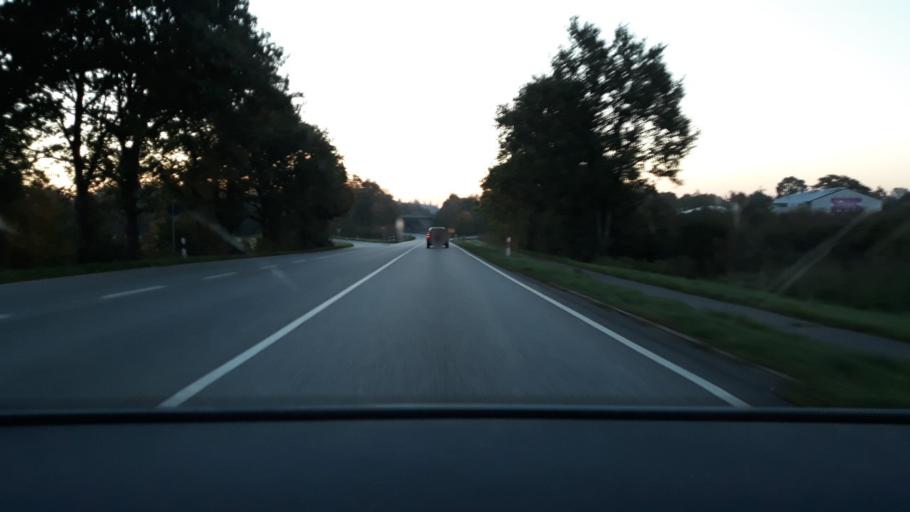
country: DE
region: Schleswig-Holstein
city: Busdorf
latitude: 54.4820
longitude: 9.5428
